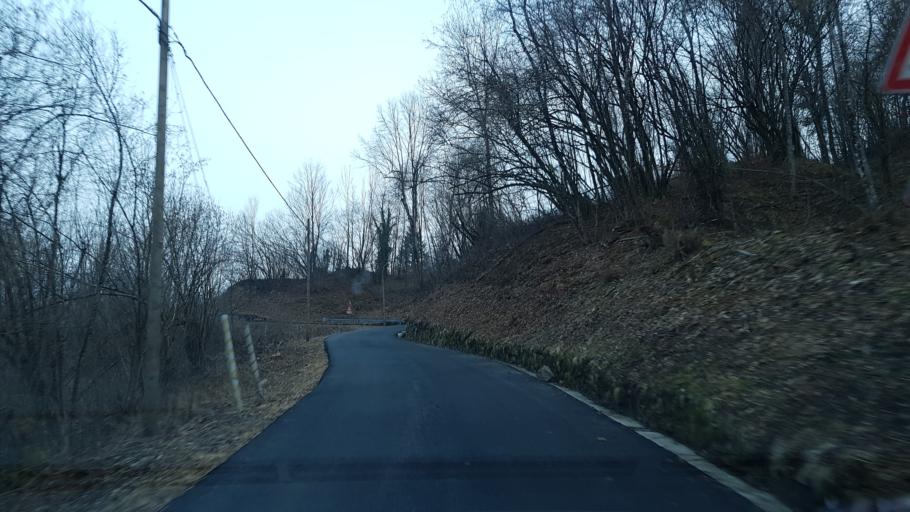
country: IT
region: Friuli Venezia Giulia
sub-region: Provincia di Udine
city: Taipana
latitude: 46.2386
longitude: 13.4082
